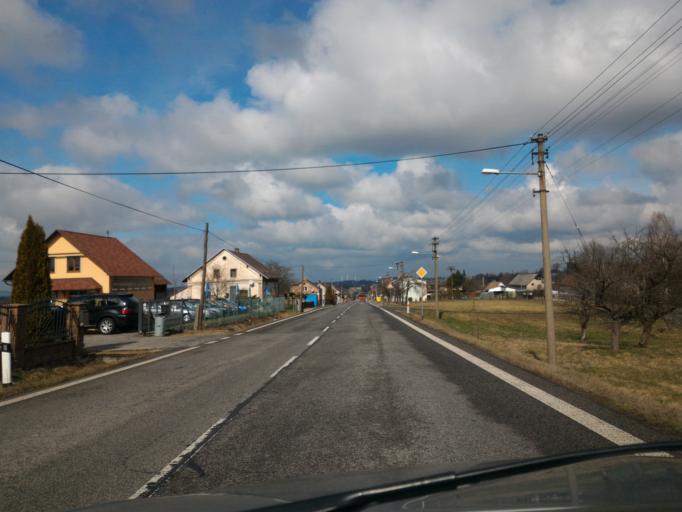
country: PL
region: Silesian Voivodeship
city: Zawidow
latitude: 51.0142
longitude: 15.0670
